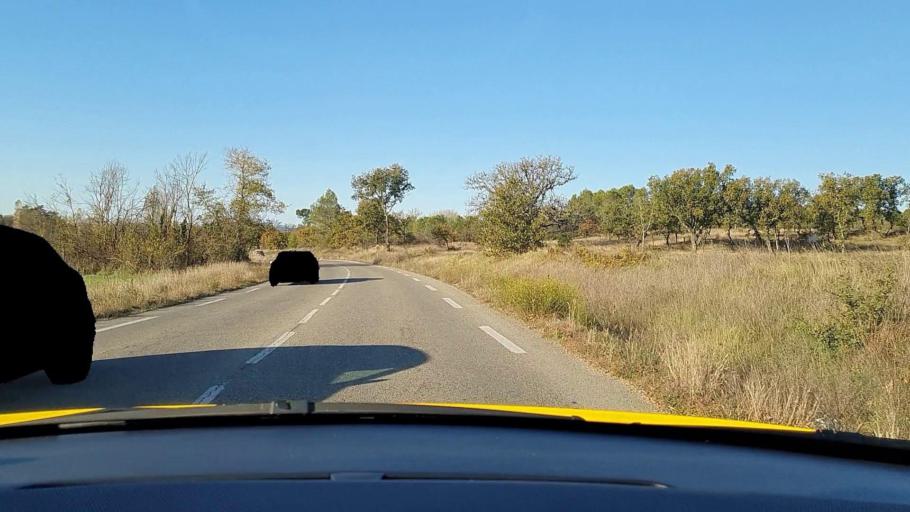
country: FR
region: Languedoc-Roussillon
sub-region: Departement du Gard
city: Salindres
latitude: 44.1855
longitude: 4.1899
